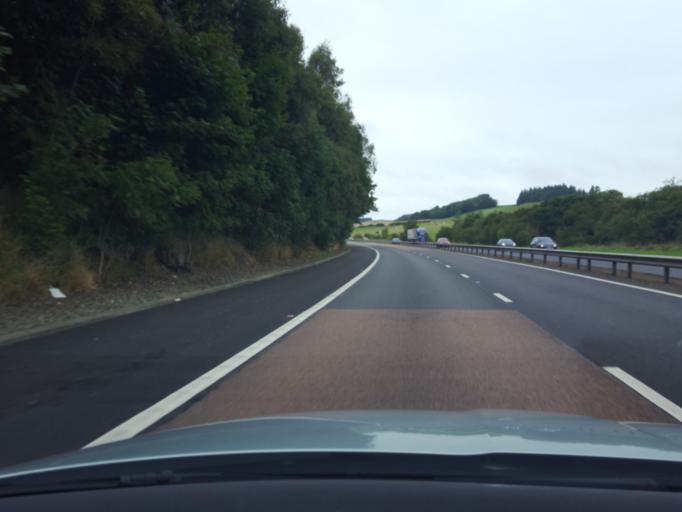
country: GB
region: Scotland
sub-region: Perth and Kinross
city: Milnathort
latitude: 56.2686
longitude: -3.3845
